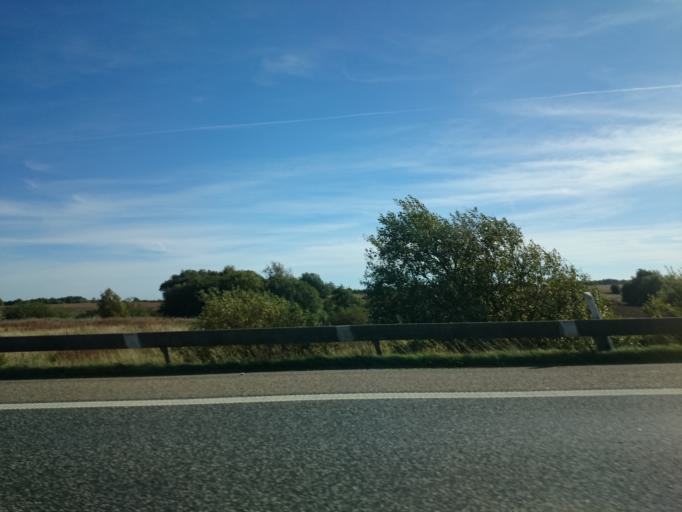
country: DK
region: Central Jutland
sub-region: Hedensted Kommune
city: Hedensted
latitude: 55.8485
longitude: 9.7424
